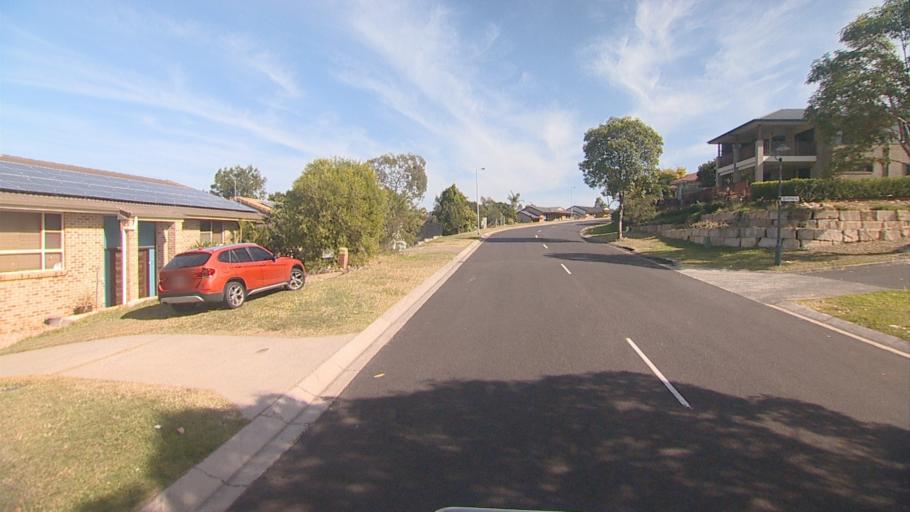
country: AU
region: Queensland
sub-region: Logan
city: Waterford West
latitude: -27.7094
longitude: 153.1638
